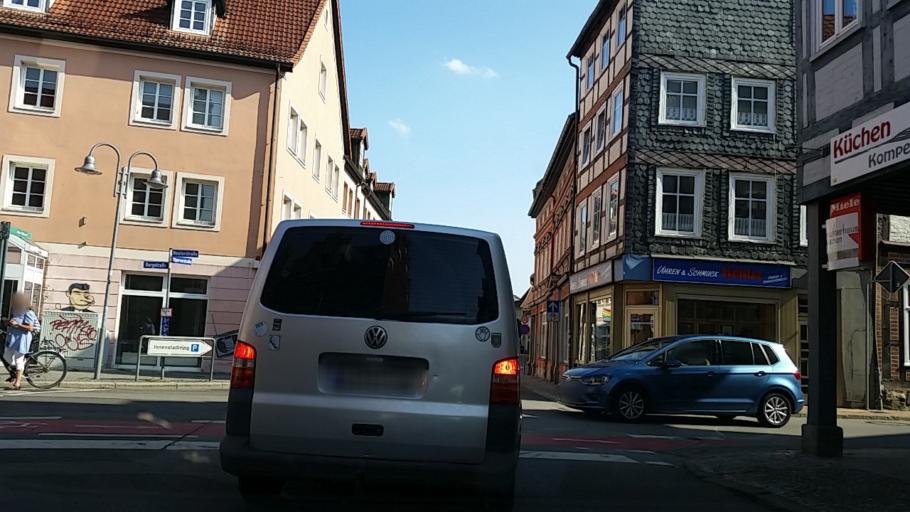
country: DE
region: Saxony-Anhalt
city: Salzwedel
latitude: 52.8497
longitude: 11.1513
